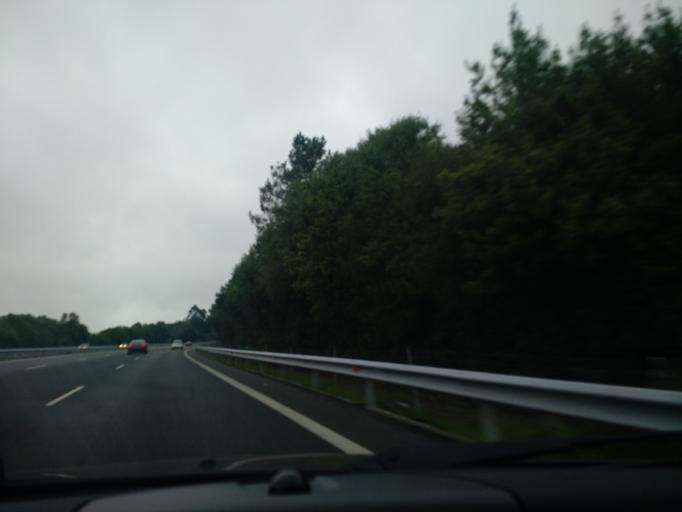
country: ES
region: Galicia
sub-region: Provincia da Coruna
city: Abegondo
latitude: 43.1762
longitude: -8.3120
